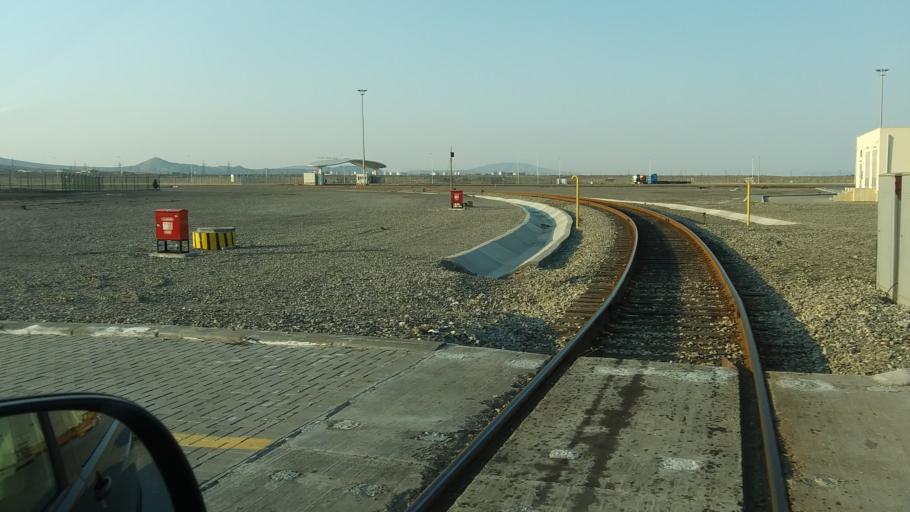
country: AZ
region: Baki
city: Qobustan
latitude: 39.9786
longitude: 49.4483
